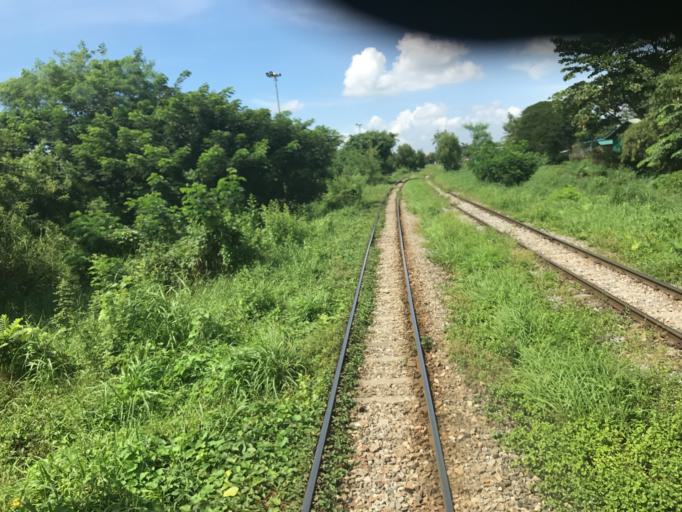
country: MM
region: Yangon
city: Yangon
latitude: 16.9089
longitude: 96.0927
